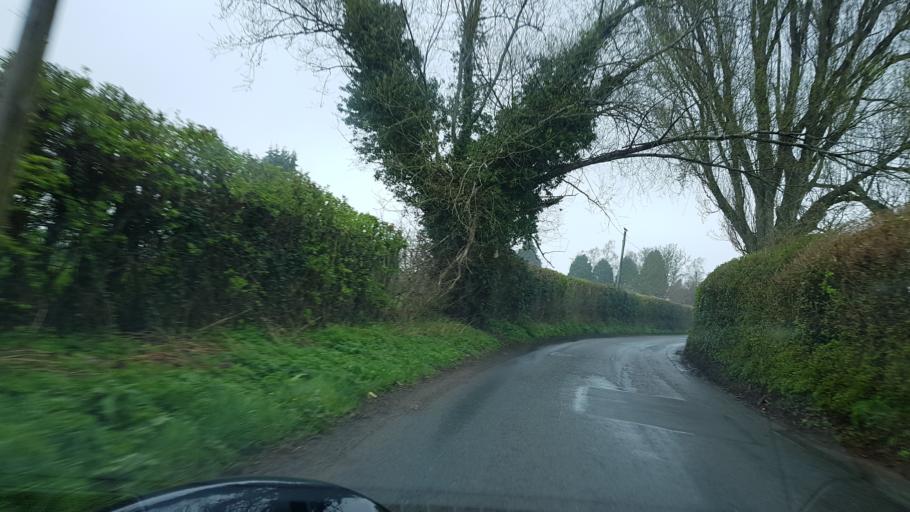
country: GB
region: England
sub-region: Herefordshire
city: Sellack
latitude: 51.9312
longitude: -2.6329
